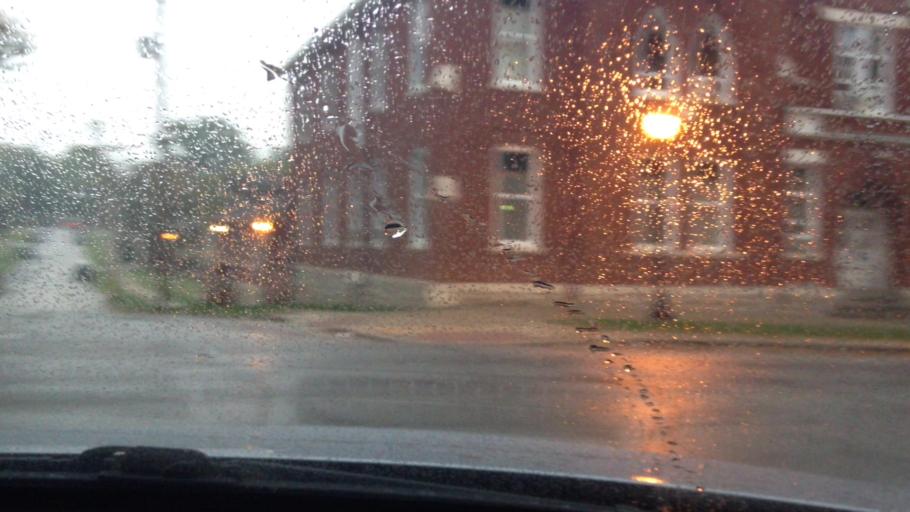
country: US
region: Kansas
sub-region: Leavenworth County
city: Leavenworth
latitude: 39.3207
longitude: -94.9221
